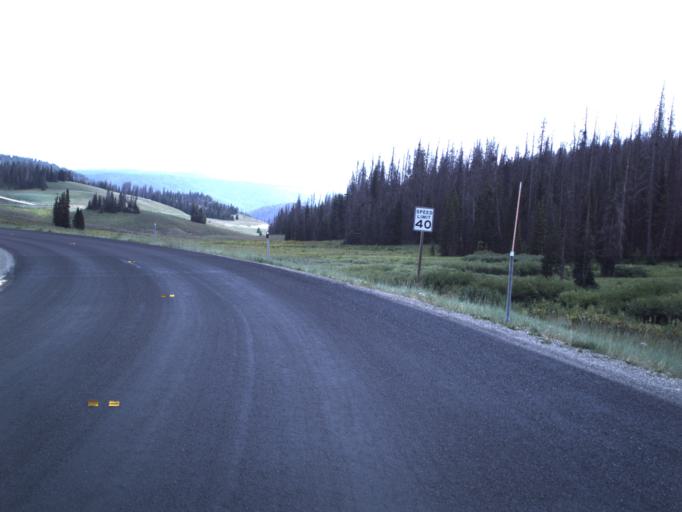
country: US
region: Utah
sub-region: Summit County
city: Francis
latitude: 40.4822
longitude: -111.0301
